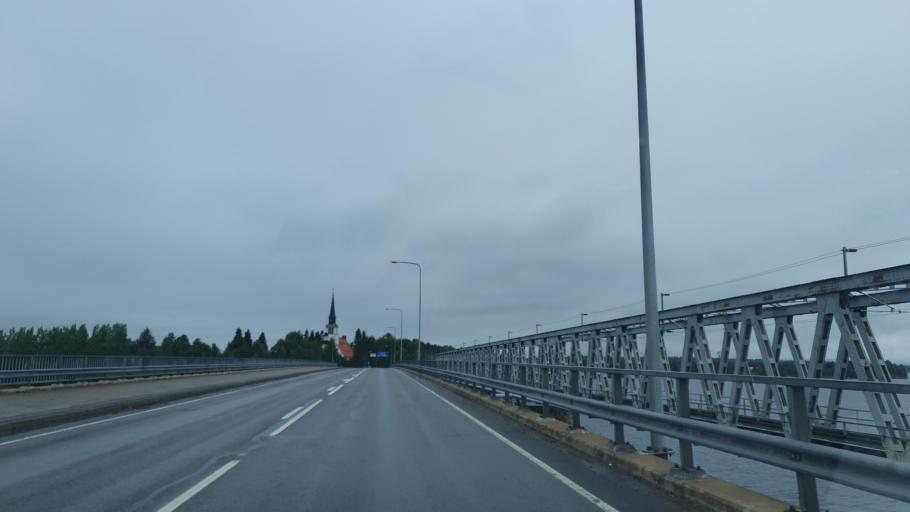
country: FI
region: Lapland
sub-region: Itae-Lappi
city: Kemijaervi
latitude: 66.7158
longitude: 27.4490
